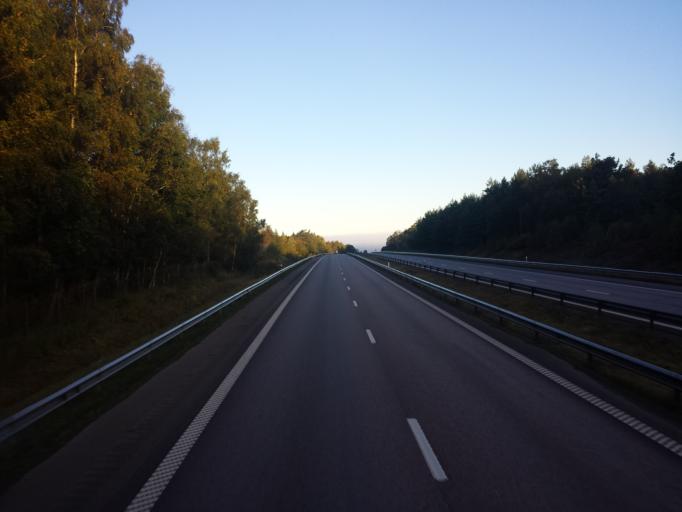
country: SE
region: Halland
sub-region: Kungsbacka Kommun
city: Kungsbacka
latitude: 57.4462
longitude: 12.1057
